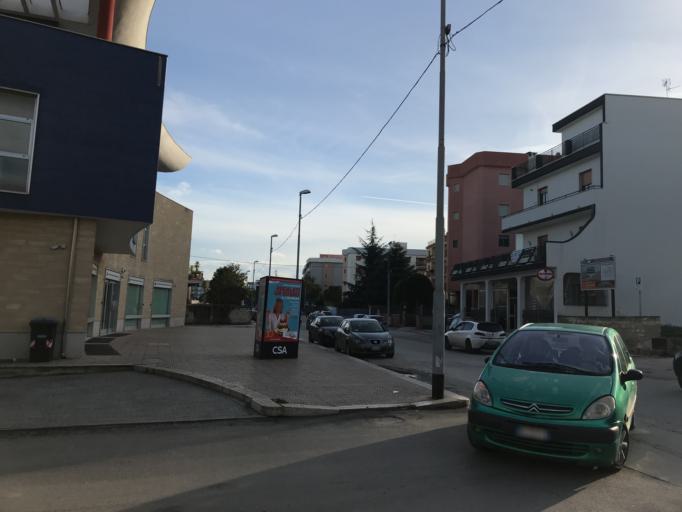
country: IT
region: Apulia
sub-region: Provincia di Bari
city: Corato
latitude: 41.1462
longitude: 16.4095
